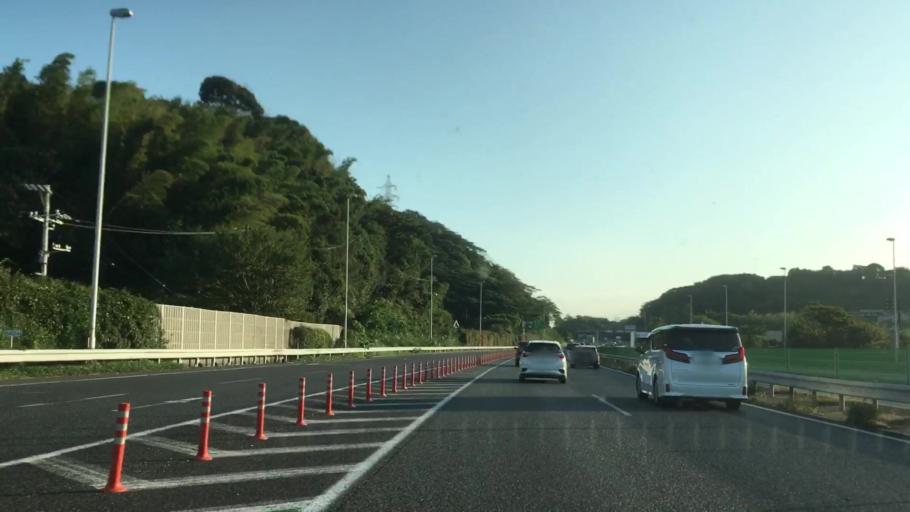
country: JP
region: Yamaguchi
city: Shimonoseki
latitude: 33.9761
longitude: 130.9520
